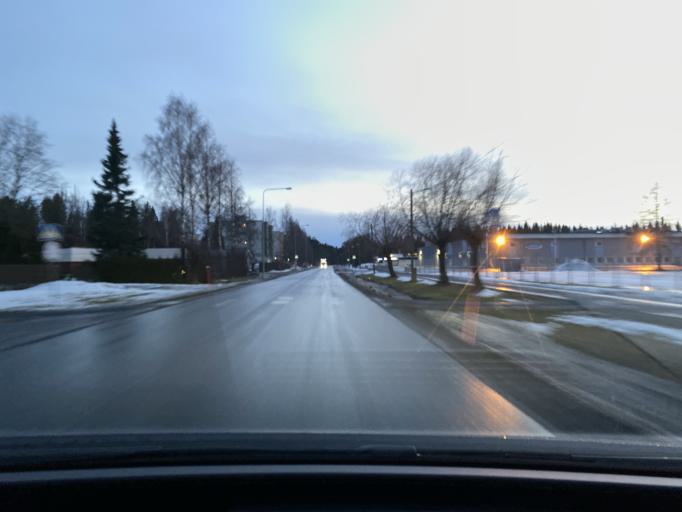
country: FI
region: Varsinais-Suomi
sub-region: Loimaa
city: Loimaa
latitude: 60.8525
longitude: 23.0415
